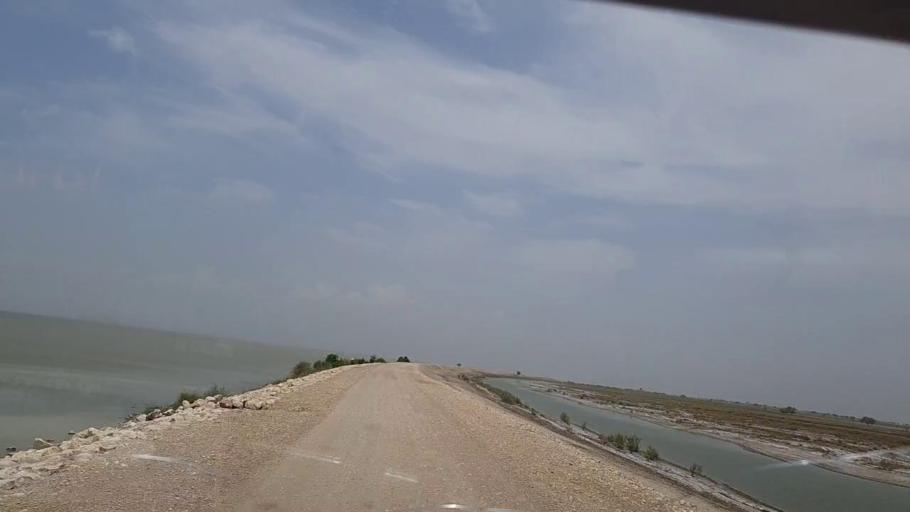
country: PK
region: Sindh
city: Sehwan
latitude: 26.4207
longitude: 67.7270
